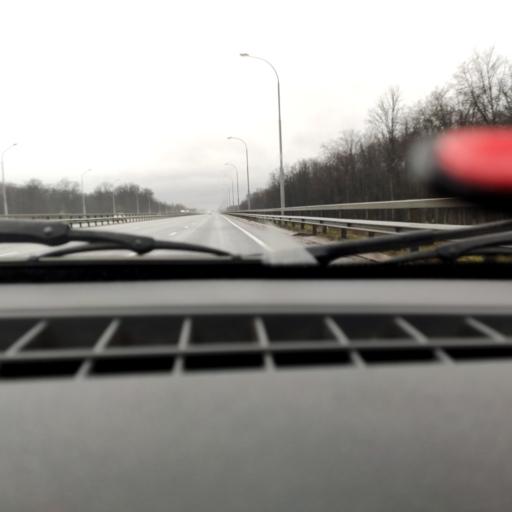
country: RU
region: Bashkortostan
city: Ufa
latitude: 54.6478
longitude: 56.0354
